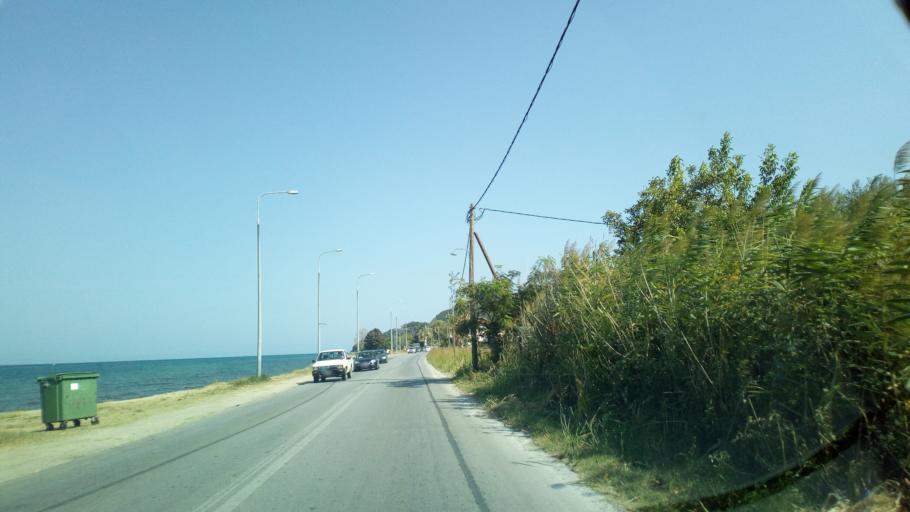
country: GR
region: Central Macedonia
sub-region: Nomos Thessalonikis
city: Stavros
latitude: 40.6615
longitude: 23.7208
